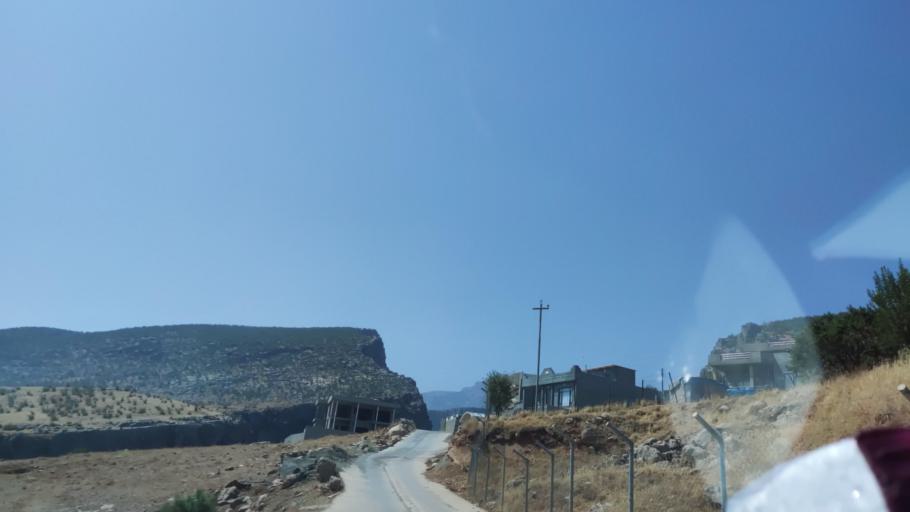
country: IQ
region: Arbil
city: Ruwandiz
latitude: 36.6499
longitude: 44.4971
